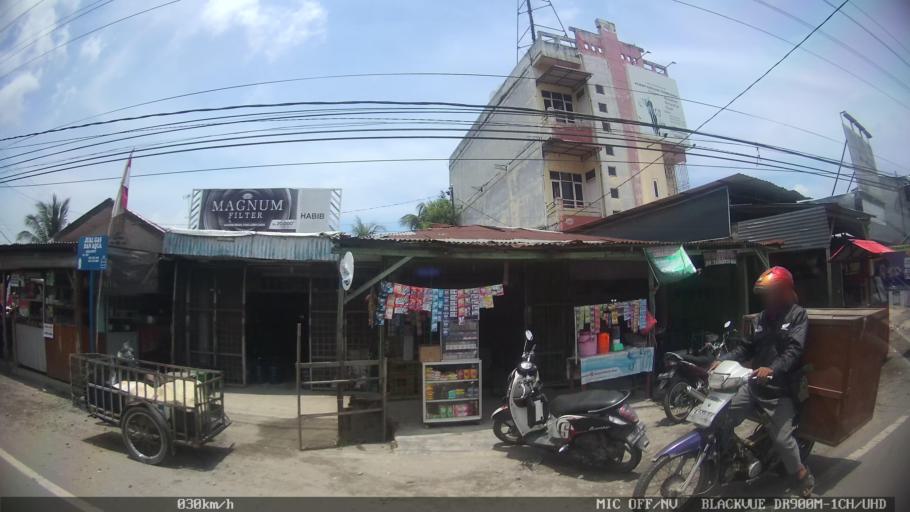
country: ID
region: North Sumatra
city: Labuhan Deli
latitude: 3.7143
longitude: 98.6619
